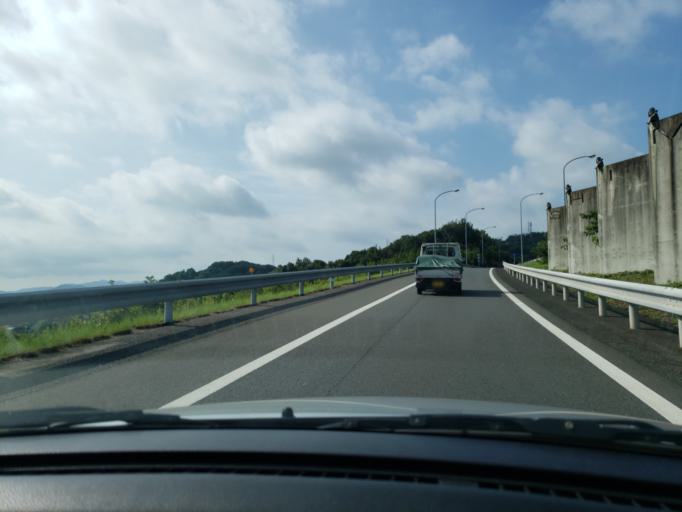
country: JP
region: Hiroshima
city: Onomichi
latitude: 34.4296
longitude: 133.2189
